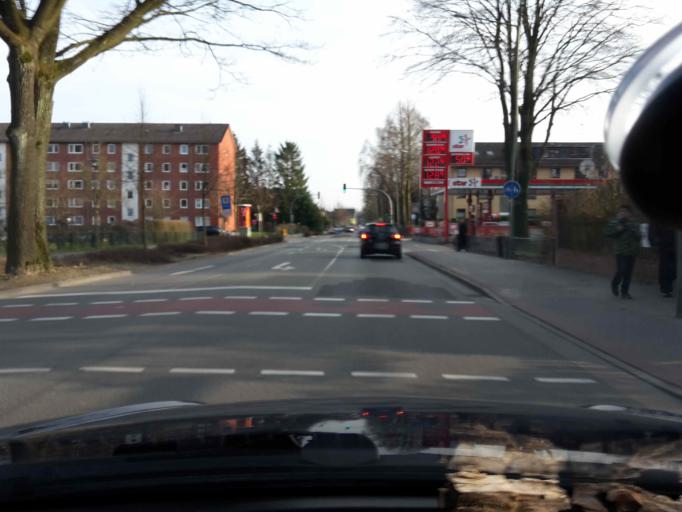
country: DE
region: Lower Saxony
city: Buchholz in der Nordheide
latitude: 53.3354
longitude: 9.8808
